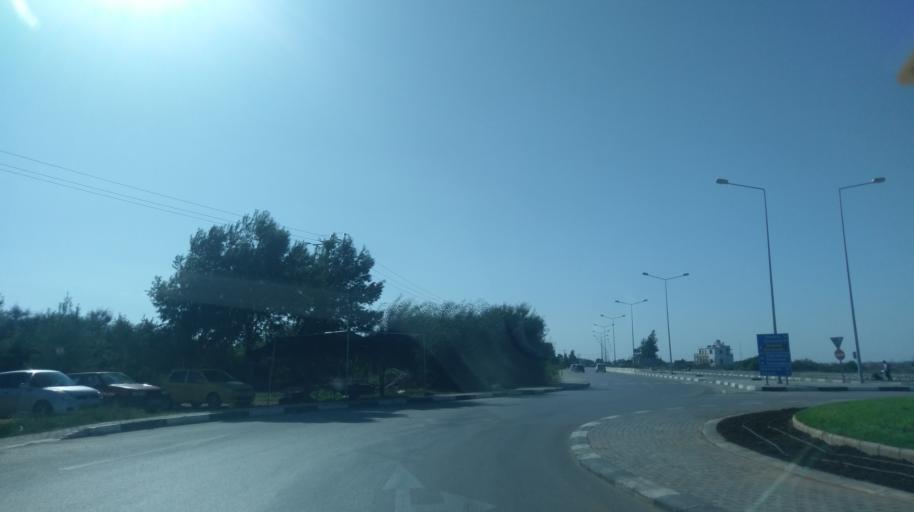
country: CY
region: Ammochostos
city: Trikomo
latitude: 35.2299
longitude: 33.8980
